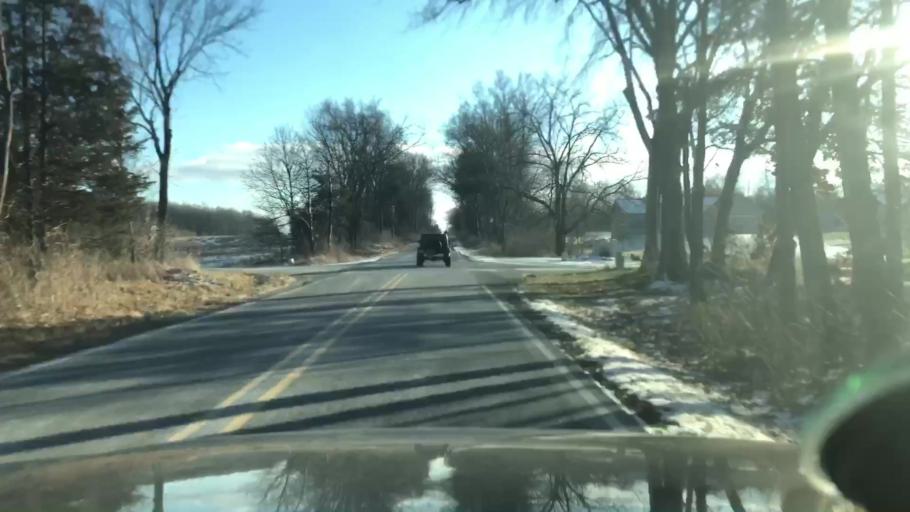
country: US
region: Michigan
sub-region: Jackson County
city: Vandercook Lake
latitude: 42.1306
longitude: -84.4516
